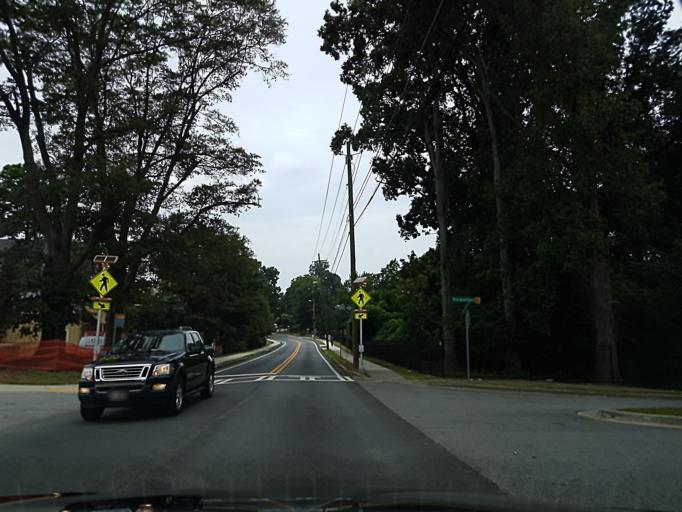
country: US
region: Georgia
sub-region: DeKalb County
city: North Atlanta
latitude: 33.8478
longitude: -84.3293
